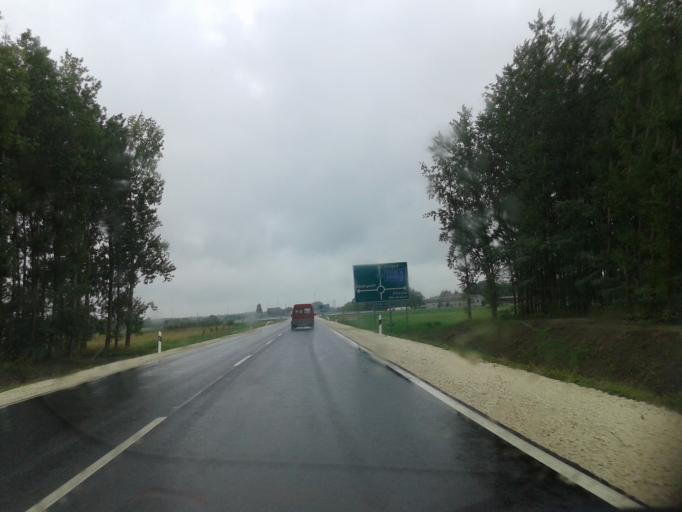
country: HU
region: Csongrad
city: Morahalom
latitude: 46.2366
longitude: 19.8681
